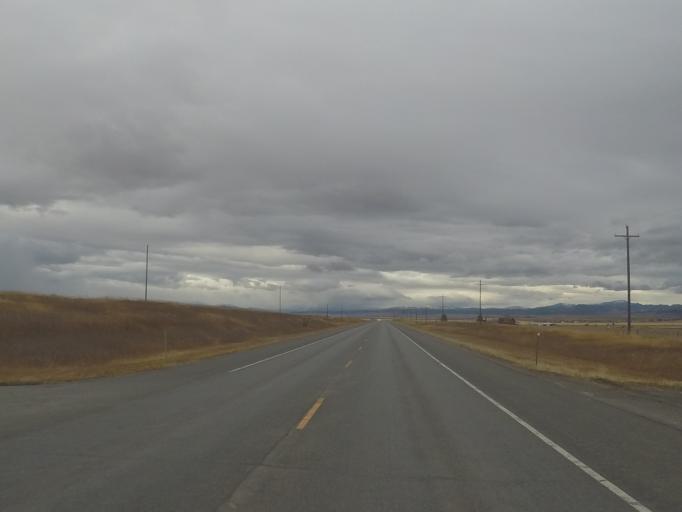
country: US
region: Montana
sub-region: Lewis and Clark County
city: East Helena
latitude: 46.5562
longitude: -111.7735
